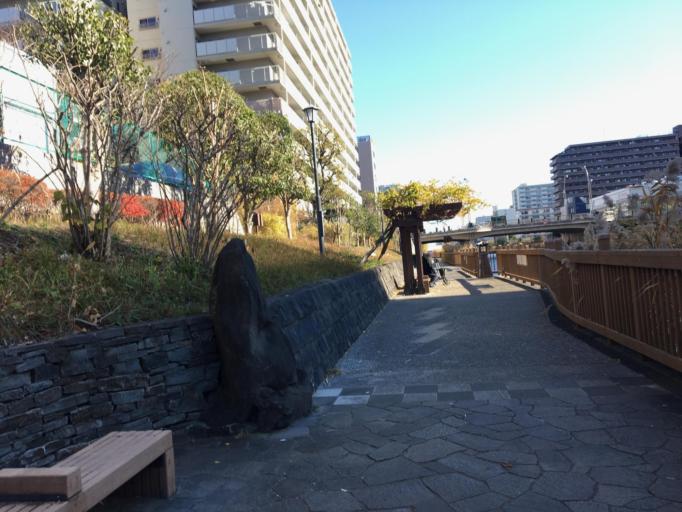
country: JP
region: Tokyo
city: Urayasu
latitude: 35.6848
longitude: 139.8146
